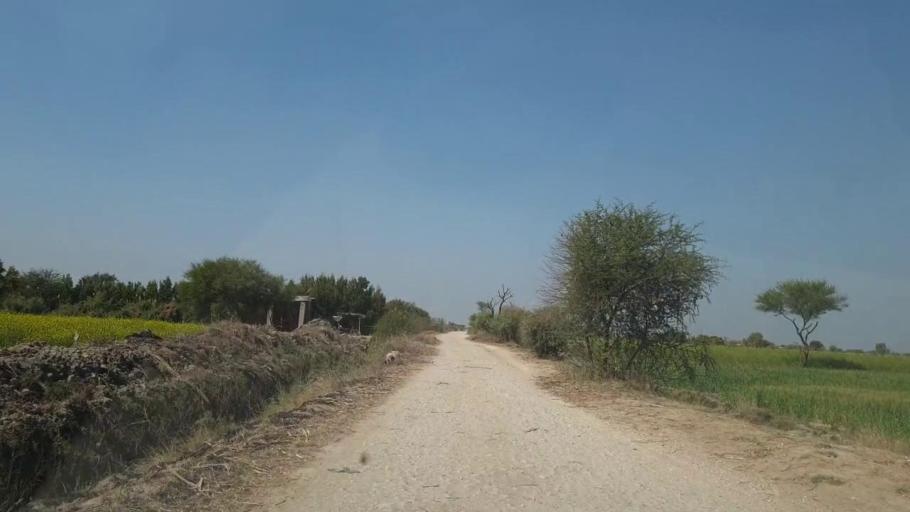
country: PK
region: Sindh
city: Mirpur Khas
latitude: 25.7278
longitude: 69.0695
